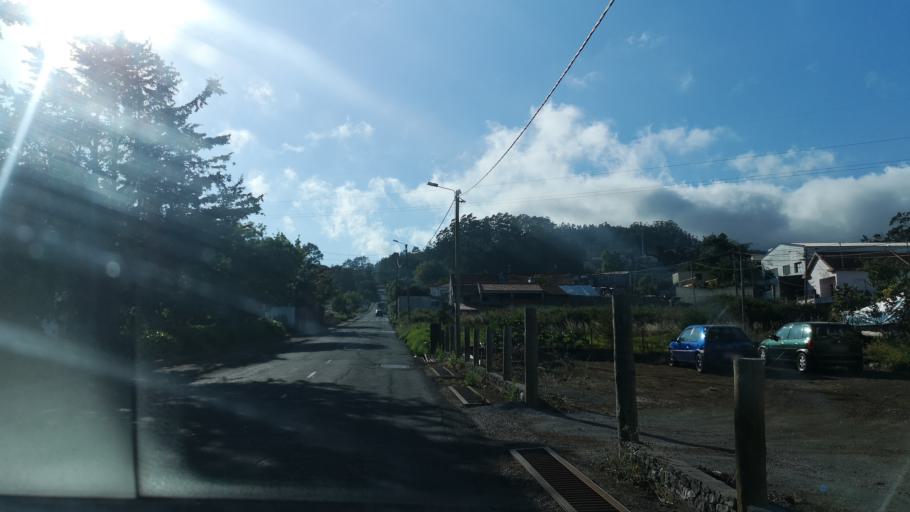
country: PT
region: Madeira
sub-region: Santa Cruz
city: Camacha
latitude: 32.6706
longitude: -16.8461
